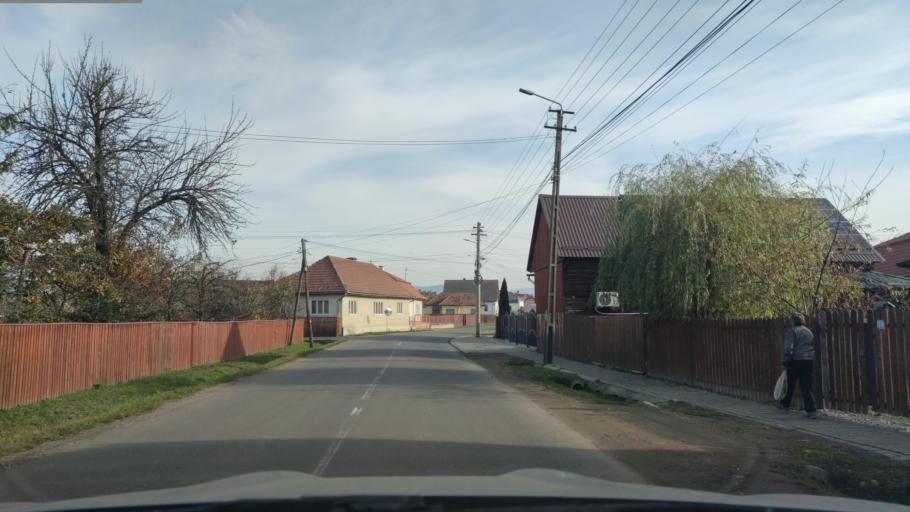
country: RO
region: Harghita
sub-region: Comuna Ditrau
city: Ditrau
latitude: 46.8062
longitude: 25.4989
